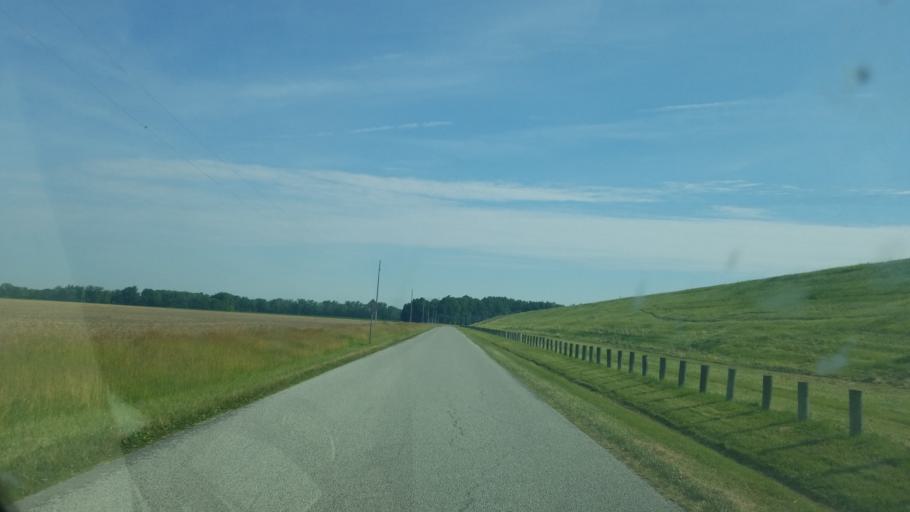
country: US
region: Ohio
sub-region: Hancock County
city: Findlay
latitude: 41.0227
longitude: -83.5807
